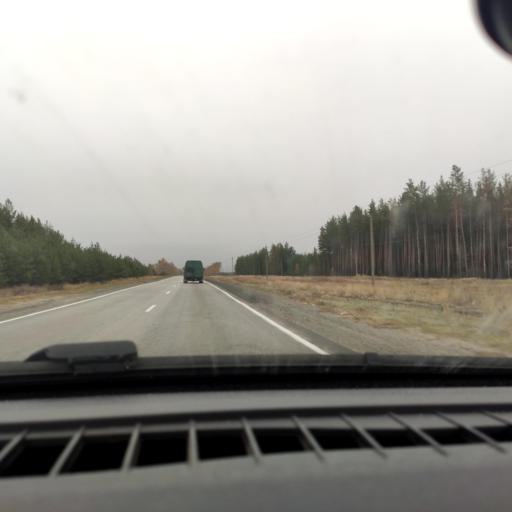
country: RU
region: Voronezj
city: Uryv-Pokrovka
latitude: 51.0557
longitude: 38.9886
